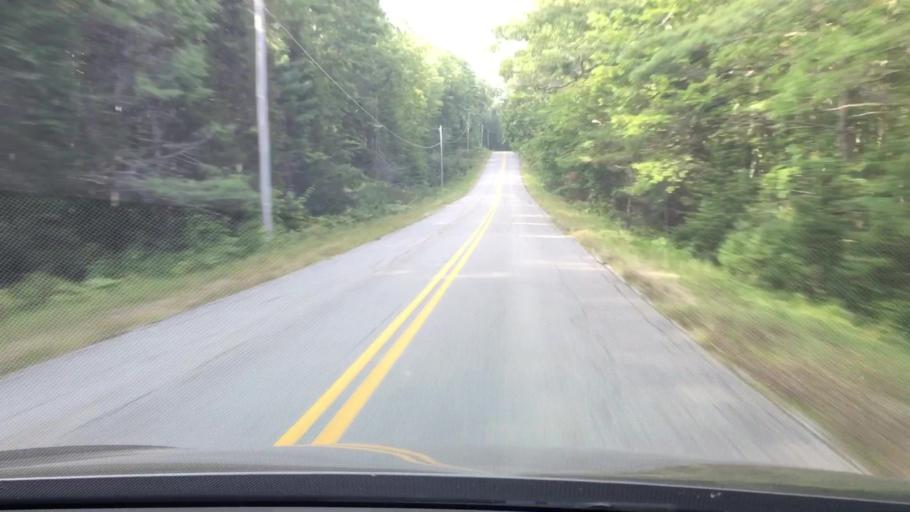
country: US
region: Maine
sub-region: Hancock County
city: Orland
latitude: 44.5263
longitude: -68.7638
